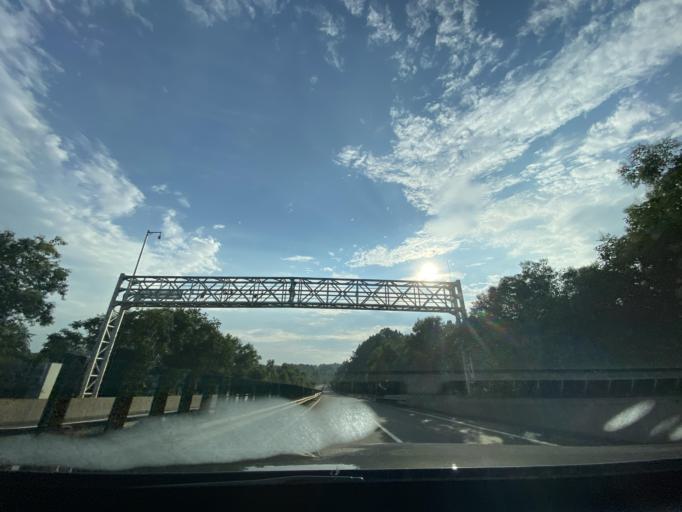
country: CN
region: Sichuan
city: Jiancheng
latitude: 30.3544
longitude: 104.5434
